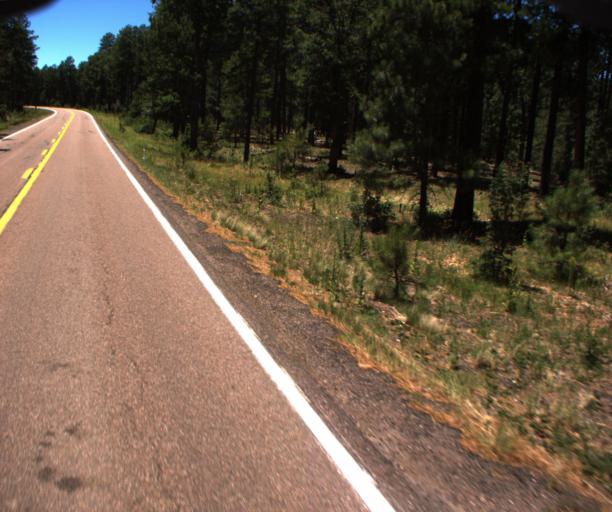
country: US
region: Arizona
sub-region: Gila County
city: Pine
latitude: 34.4548
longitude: -111.4138
